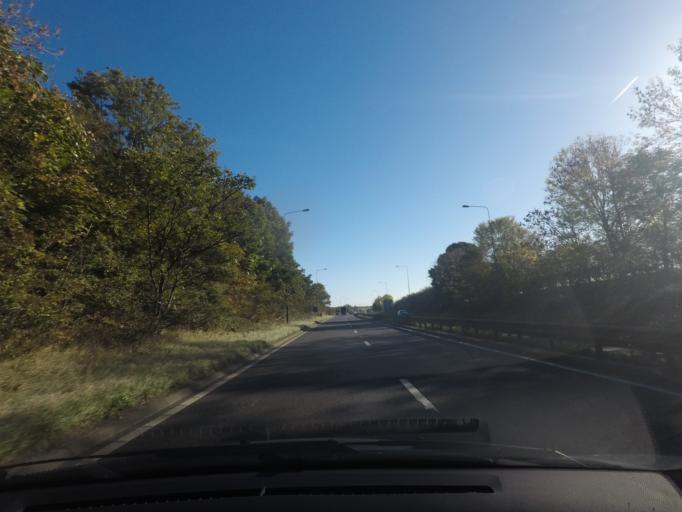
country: GB
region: England
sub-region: East Riding of Yorkshire
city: North Ferriby
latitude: 53.7263
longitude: -0.5002
